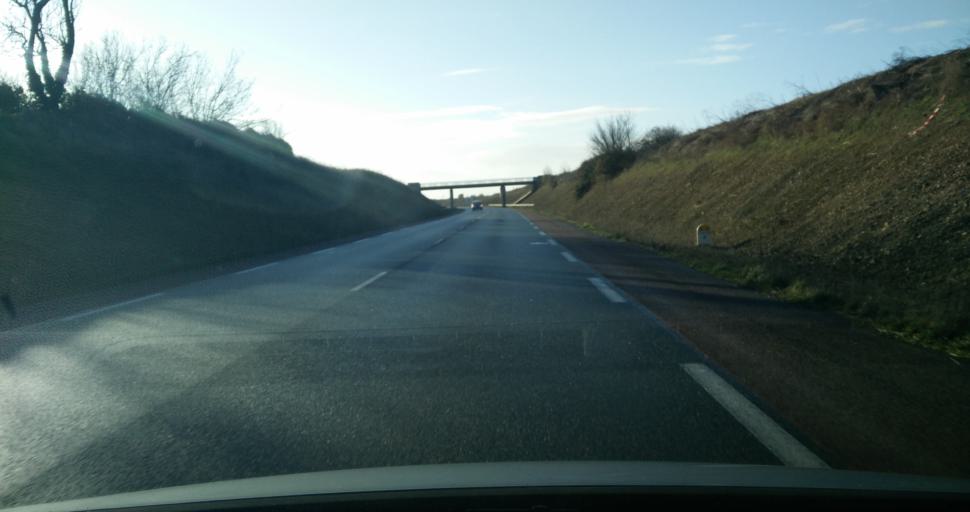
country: FR
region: Poitou-Charentes
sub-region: Departement de la Charente-Maritime
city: Saint-Xandre
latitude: 46.1870
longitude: -1.0936
